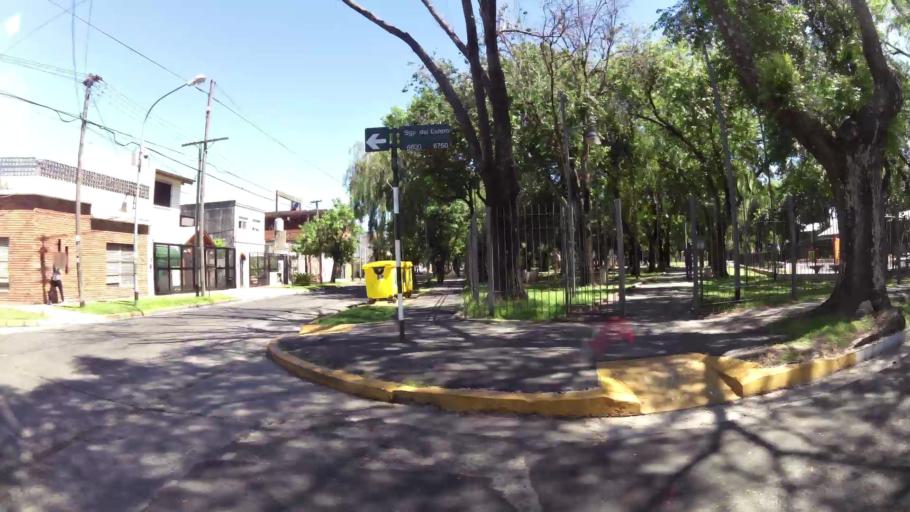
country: AR
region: Buenos Aires
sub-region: Partido de General San Martin
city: General San Martin
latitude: -34.5307
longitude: -58.5505
